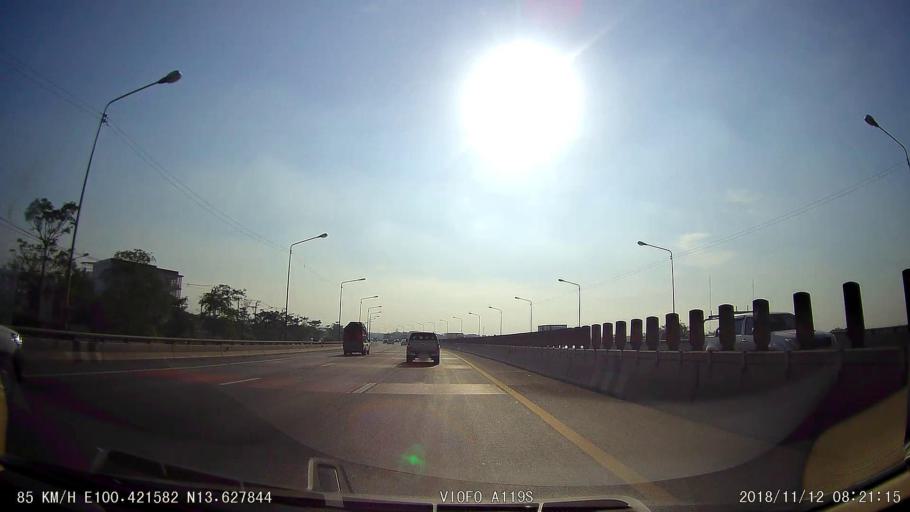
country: TH
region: Bangkok
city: Bang Khun Thian
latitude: 13.6278
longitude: 100.4218
